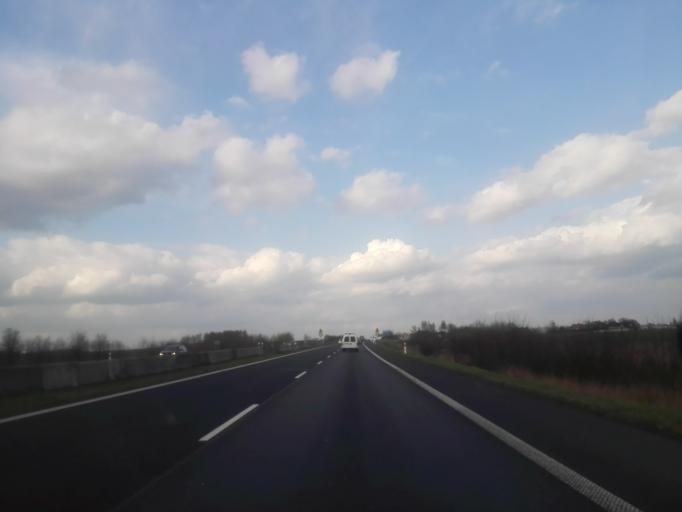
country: PL
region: Silesian Voivodeship
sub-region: Powiat czestochowski
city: Borowno
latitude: 50.9505
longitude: 19.2425
